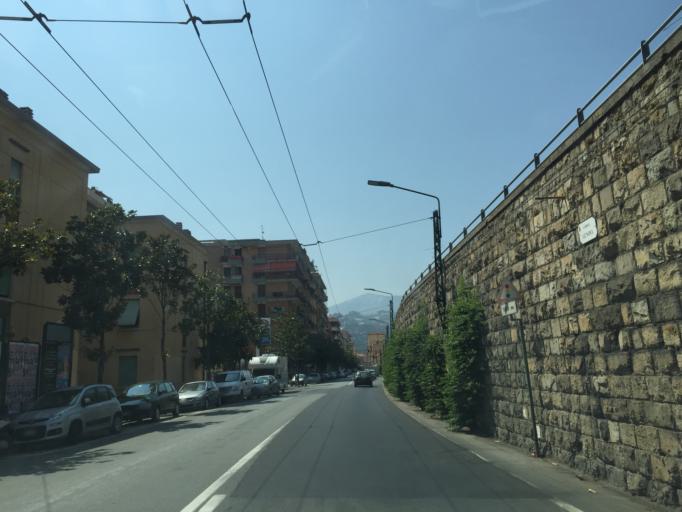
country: IT
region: Liguria
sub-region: Provincia di Imperia
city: Ventimiglia
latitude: 43.7892
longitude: 7.6185
